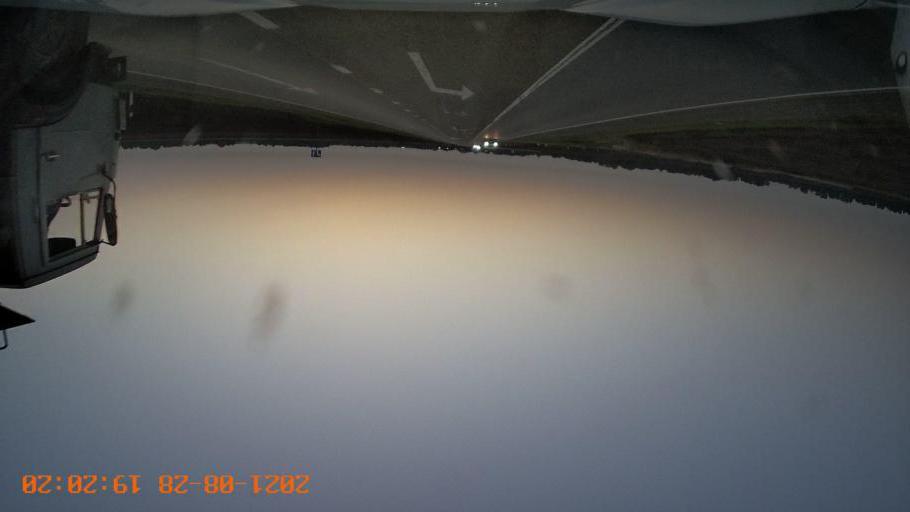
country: RU
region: Krasnodarskiy
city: Ryazanskaya
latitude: 44.8908
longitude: 39.5053
